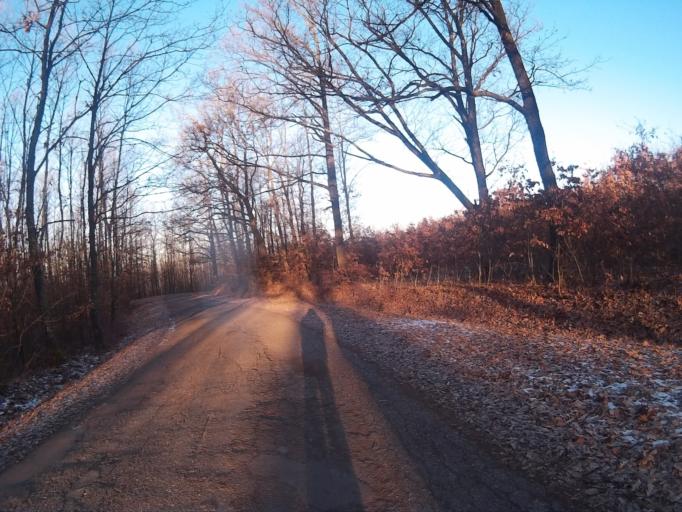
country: HU
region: Borsod-Abauj-Zemplen
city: Putnok
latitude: 48.3491
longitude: 20.4385
